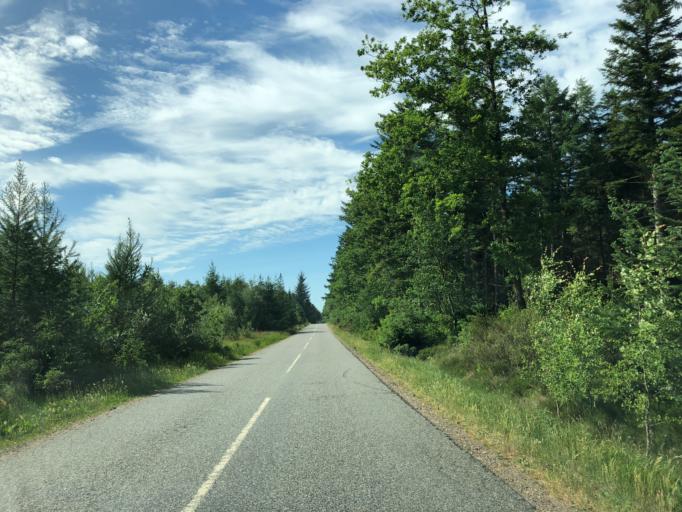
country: DK
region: Central Jutland
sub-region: Herning Kommune
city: Lind
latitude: 56.0275
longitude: 8.9559
